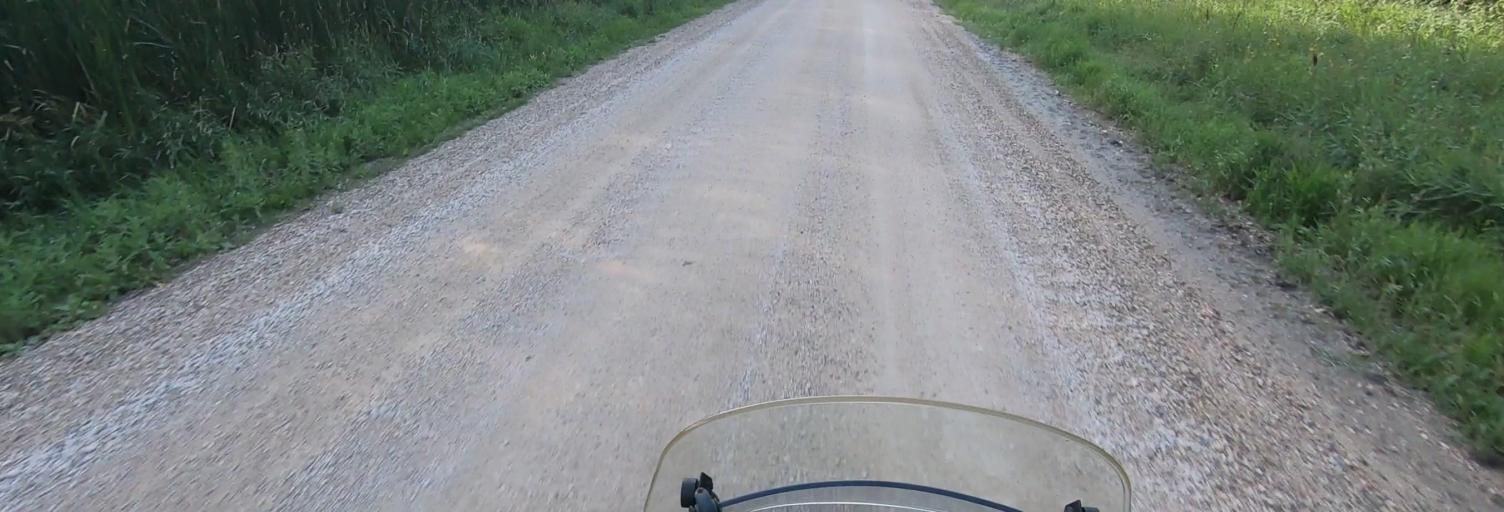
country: CA
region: Manitoba
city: Selkirk
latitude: 50.2839
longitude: -96.8602
